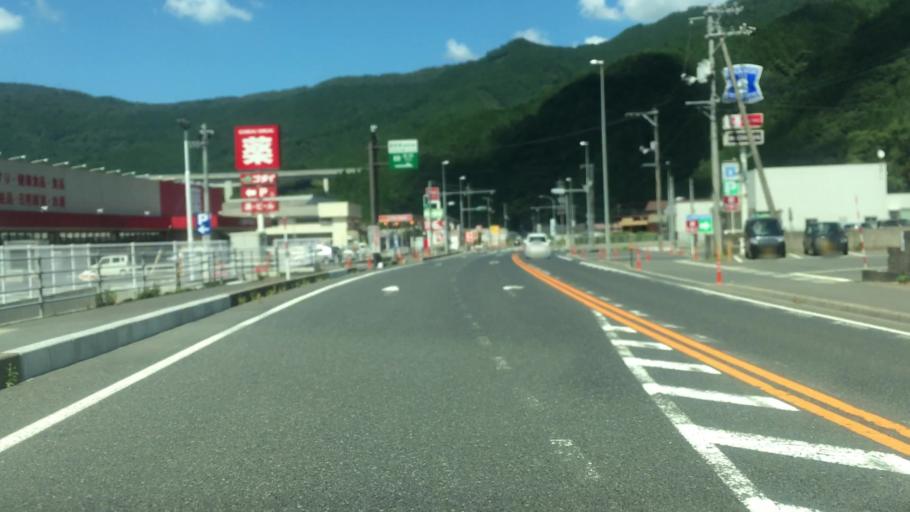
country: JP
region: Tottori
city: Tottori
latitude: 35.2773
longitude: 134.2257
